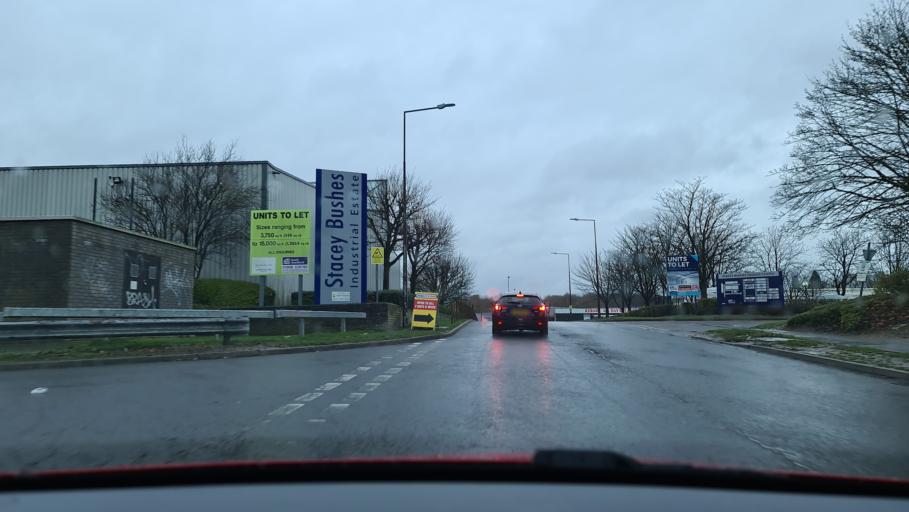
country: GB
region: England
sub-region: Milton Keynes
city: Bradwell
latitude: 52.0501
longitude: -0.7986
